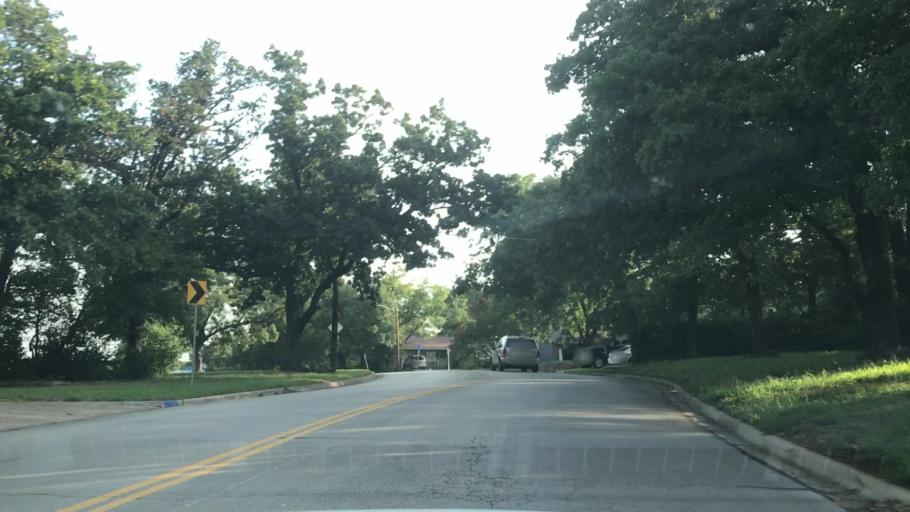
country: US
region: Texas
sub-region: Tarrant County
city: Arlington
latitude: 32.7462
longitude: -97.1232
